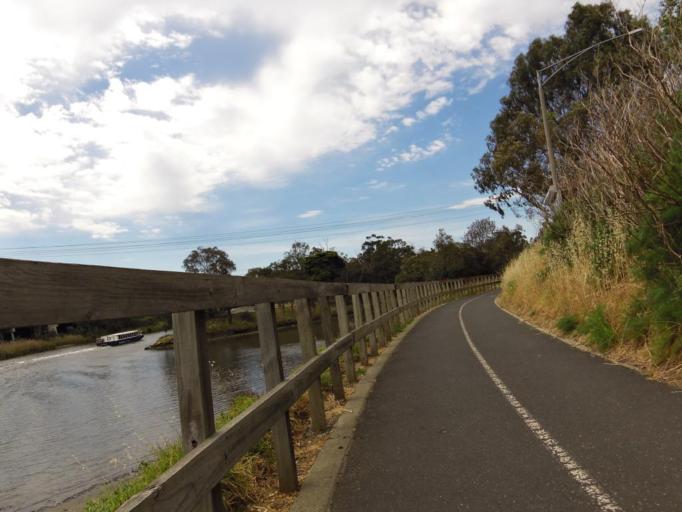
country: AU
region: Victoria
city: Albert Park
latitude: -37.8339
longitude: 145.0007
